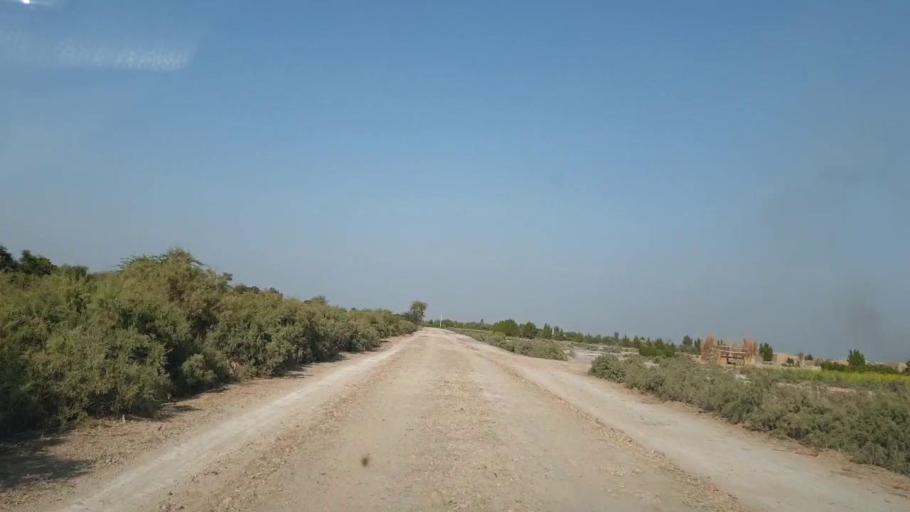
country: PK
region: Sindh
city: Tando Mittha Khan
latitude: 25.7458
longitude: 69.1947
